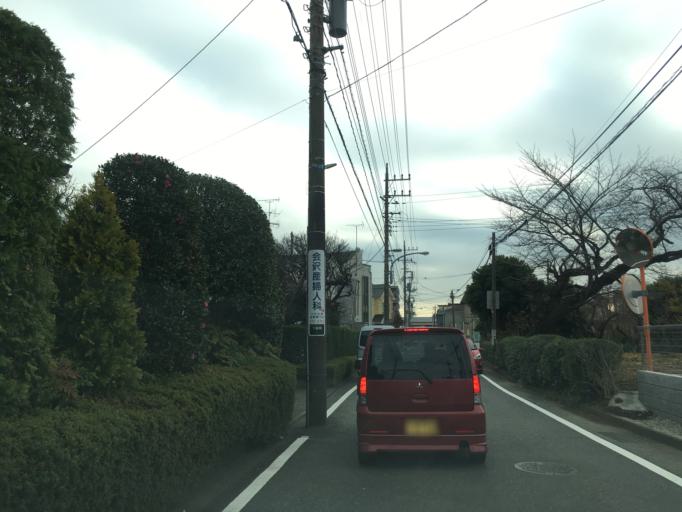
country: JP
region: Tokyo
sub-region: Machida-shi
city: Machida
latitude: 35.5155
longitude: 139.4633
